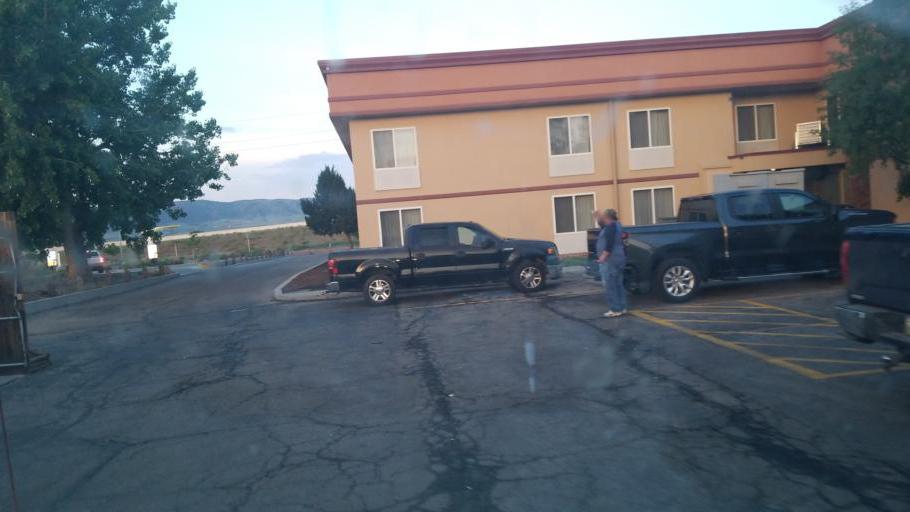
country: US
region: Wyoming
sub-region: Natrona County
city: Casper
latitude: 42.8590
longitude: -106.3319
